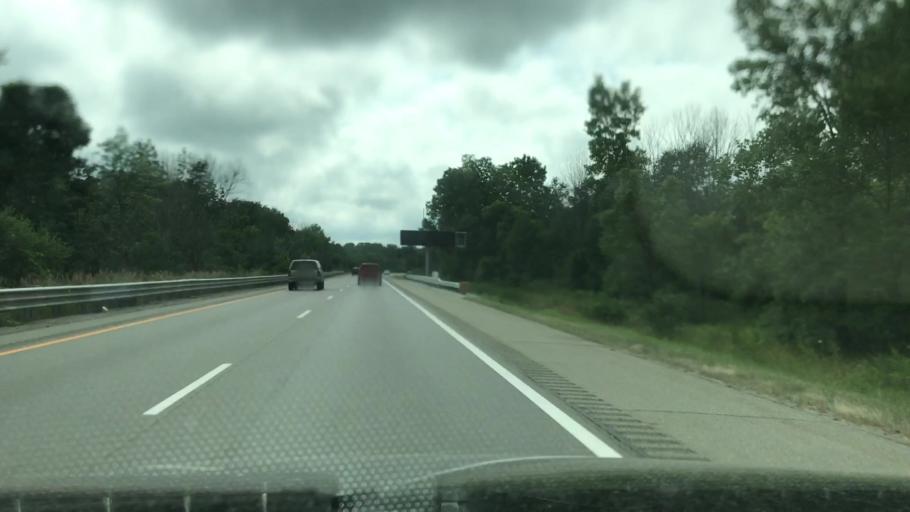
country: US
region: Michigan
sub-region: Ottawa County
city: Coopersville
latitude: 43.0711
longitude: -86.0242
